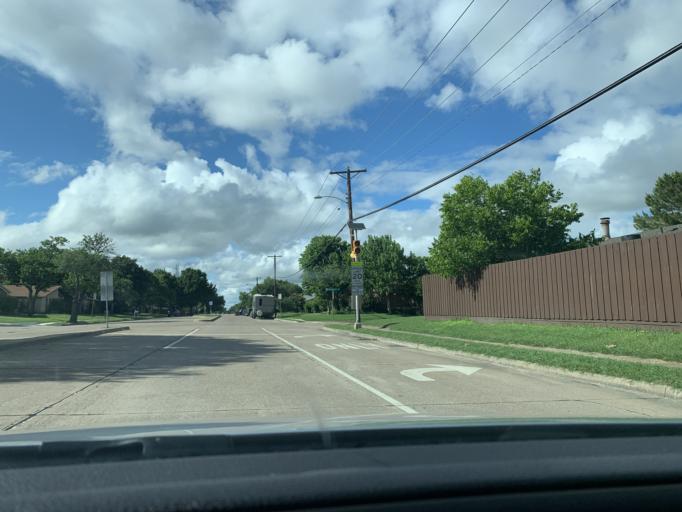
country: US
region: Texas
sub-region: Dallas County
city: Cedar Hill
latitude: 32.6530
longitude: -97.0278
